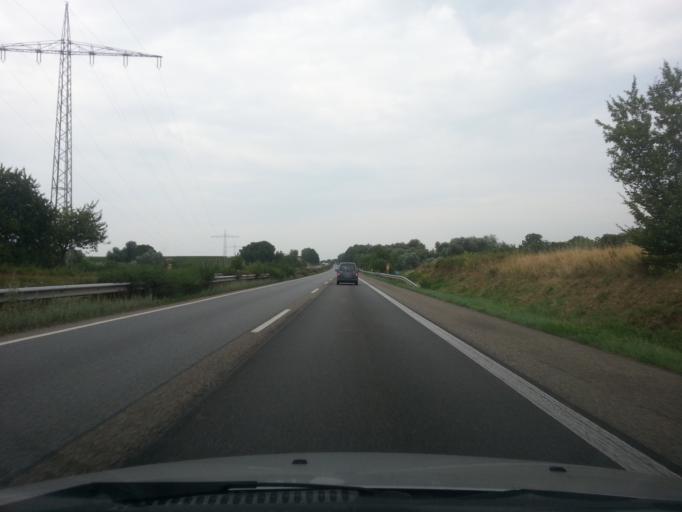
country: DE
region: Rheinland-Pfalz
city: Knoringen
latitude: 49.2539
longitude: 8.1500
